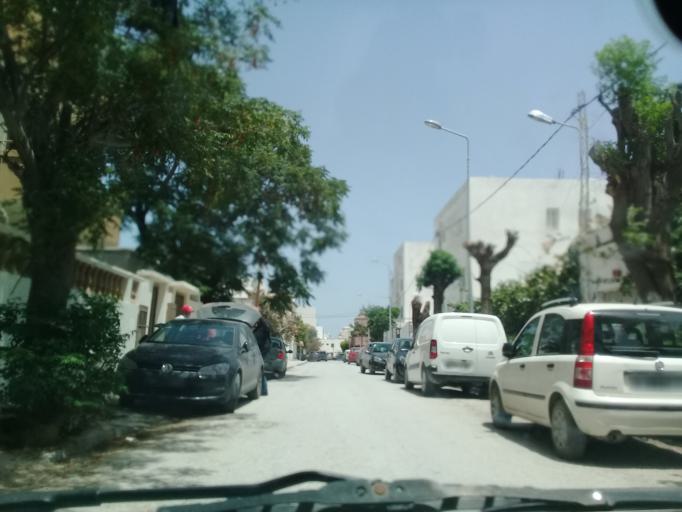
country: TN
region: Tunis
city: Tunis
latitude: 36.8295
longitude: 10.1941
